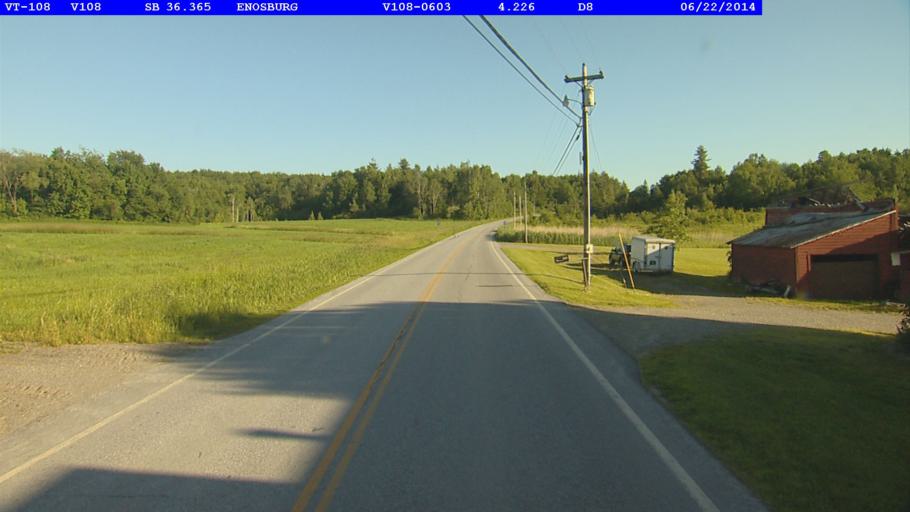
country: US
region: Vermont
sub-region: Franklin County
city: Enosburg Falls
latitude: 44.8961
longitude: -72.8005
